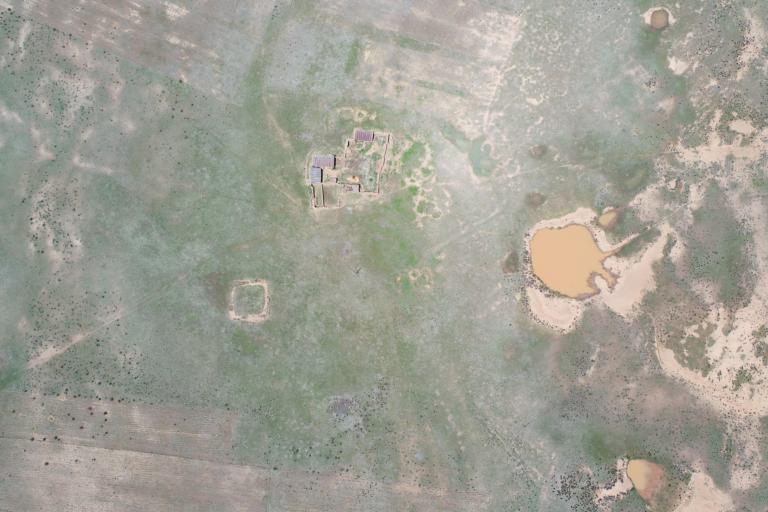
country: BO
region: La Paz
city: Curahuara de Carangas
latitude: -17.2756
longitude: -68.5176
